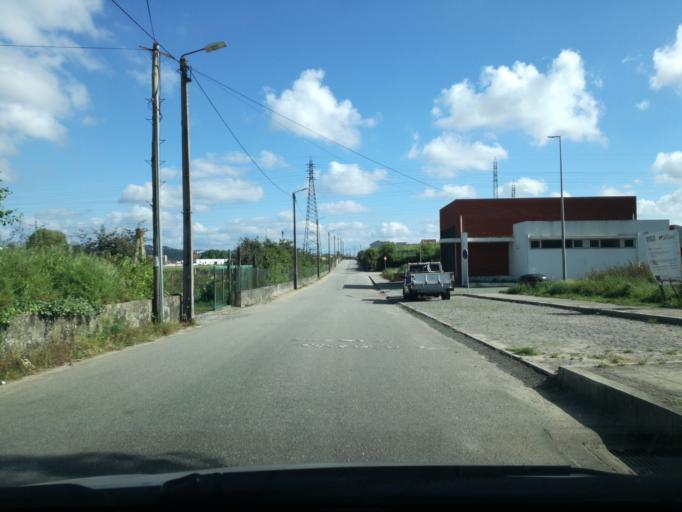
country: PT
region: Porto
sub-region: Valongo
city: Ermesinde
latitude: 41.2344
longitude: -8.5624
